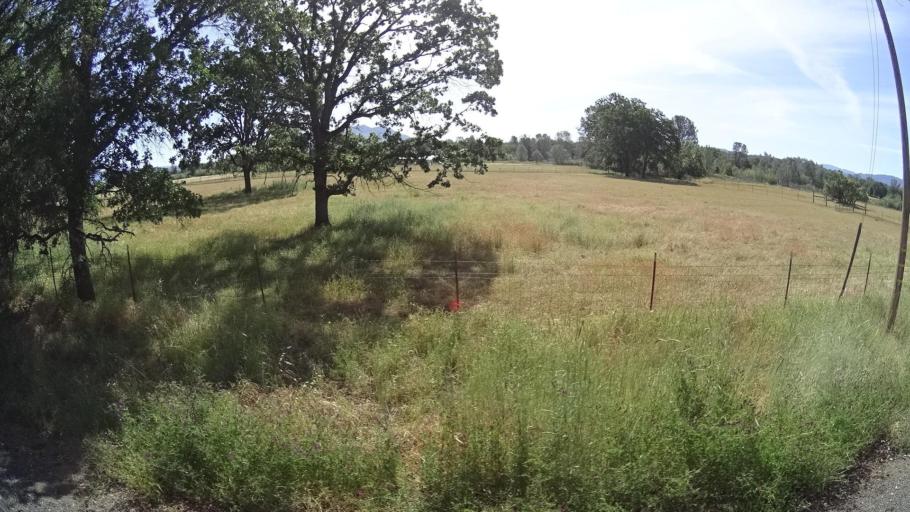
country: US
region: California
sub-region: Lake County
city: Kelseyville
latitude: 38.9530
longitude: -122.8963
